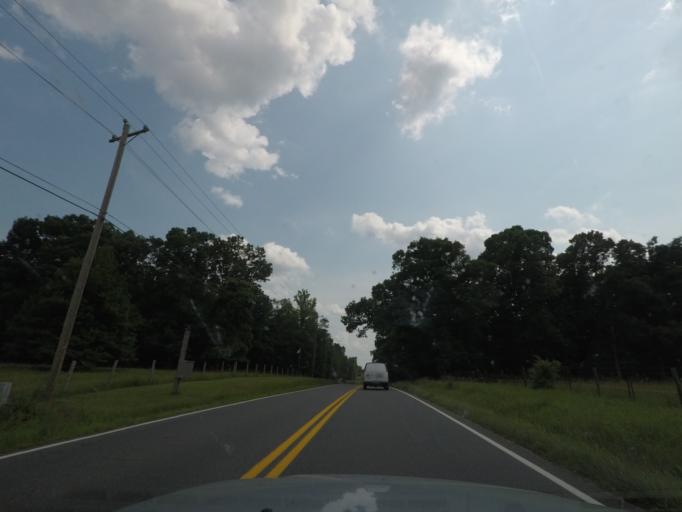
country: US
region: Virginia
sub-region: Fluvanna County
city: Palmyra
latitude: 37.9306
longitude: -78.2488
